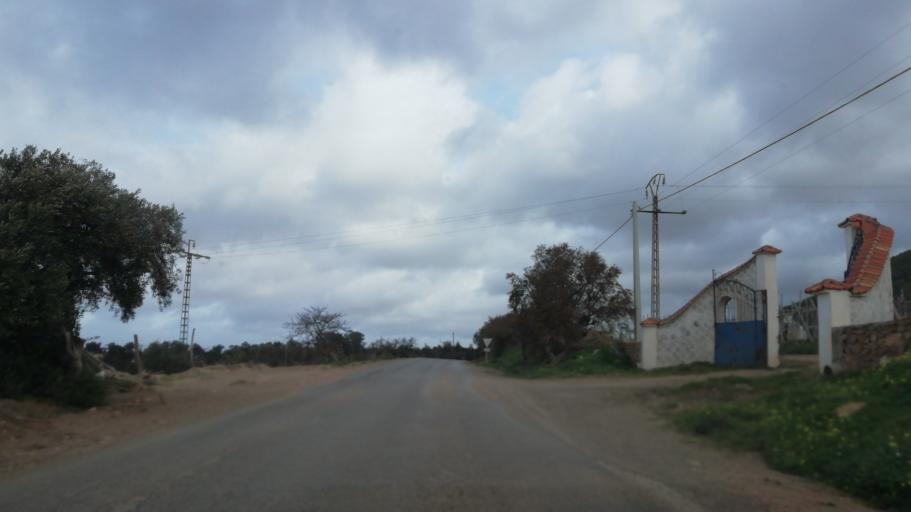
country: DZ
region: Oran
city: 'Ain el Turk
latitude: 35.7033
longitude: -0.8406
